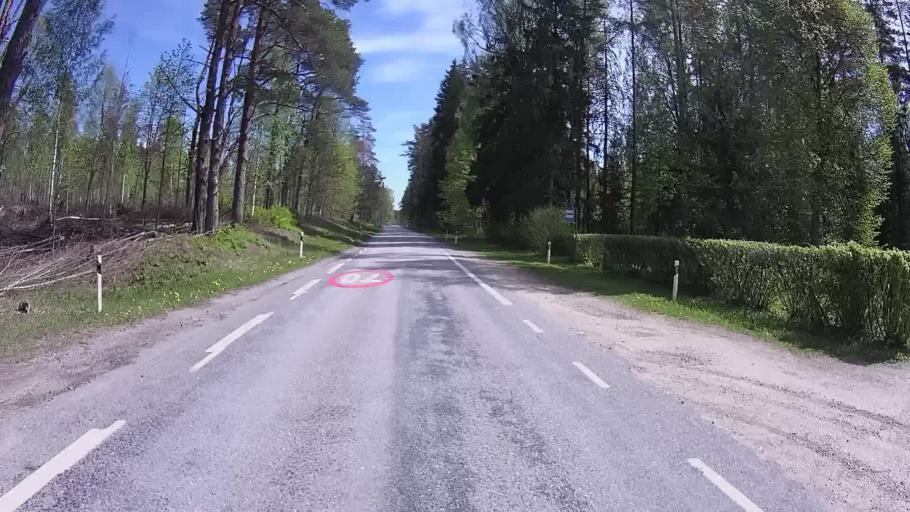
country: LV
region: Apes Novads
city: Ape
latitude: 57.6098
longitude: 26.4460
